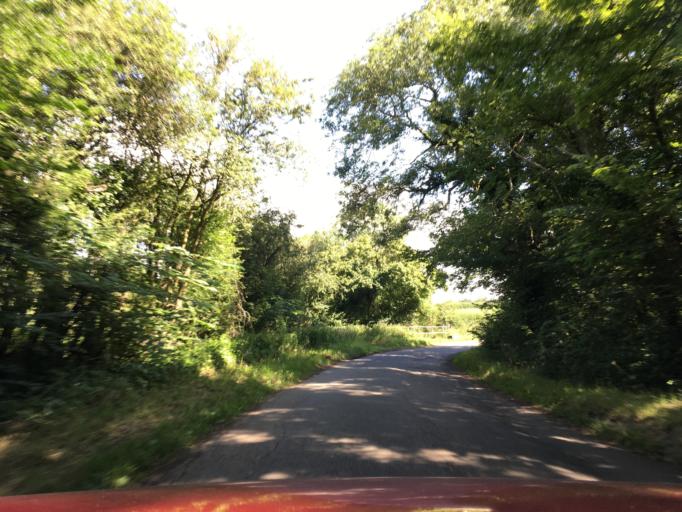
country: GB
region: England
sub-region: Milton Keynes
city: Calverton
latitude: 51.9980
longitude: -0.8698
